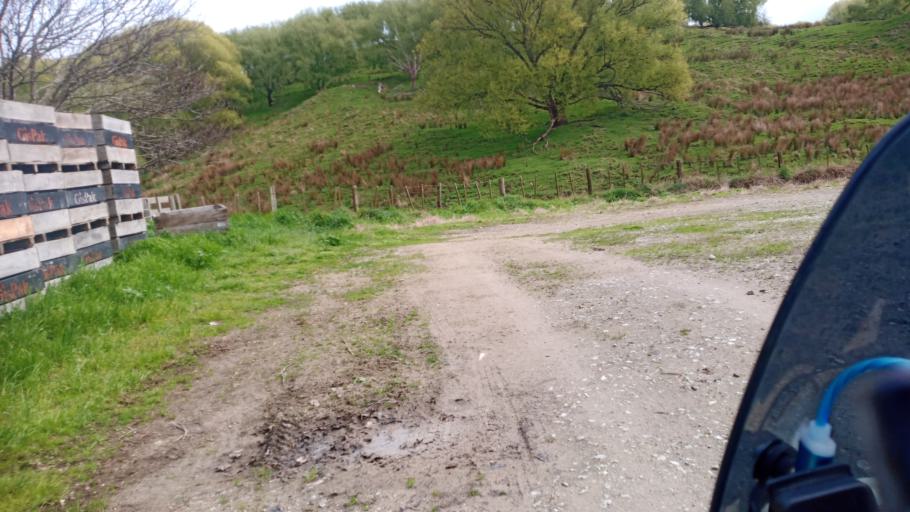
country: NZ
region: Gisborne
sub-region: Gisborne District
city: Gisborne
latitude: -38.5791
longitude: 178.1515
